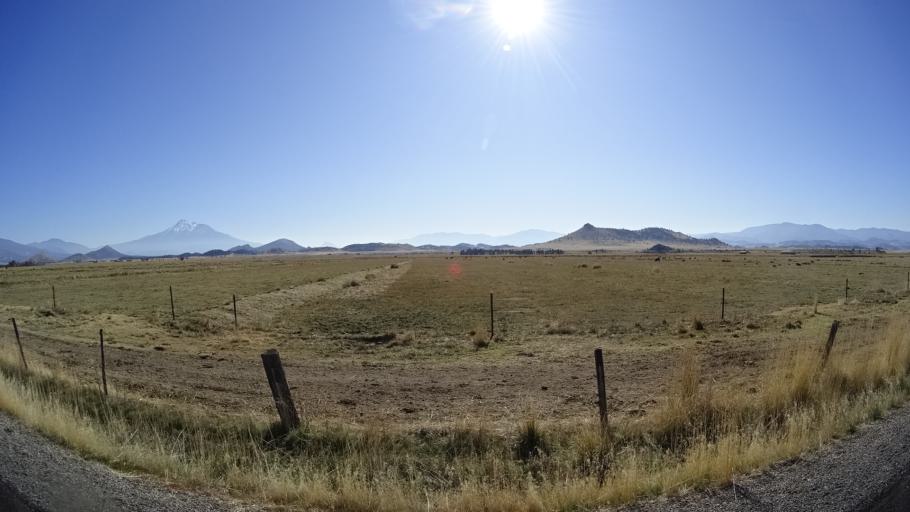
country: US
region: California
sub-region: Siskiyou County
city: Montague
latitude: 41.7242
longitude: -122.4516
